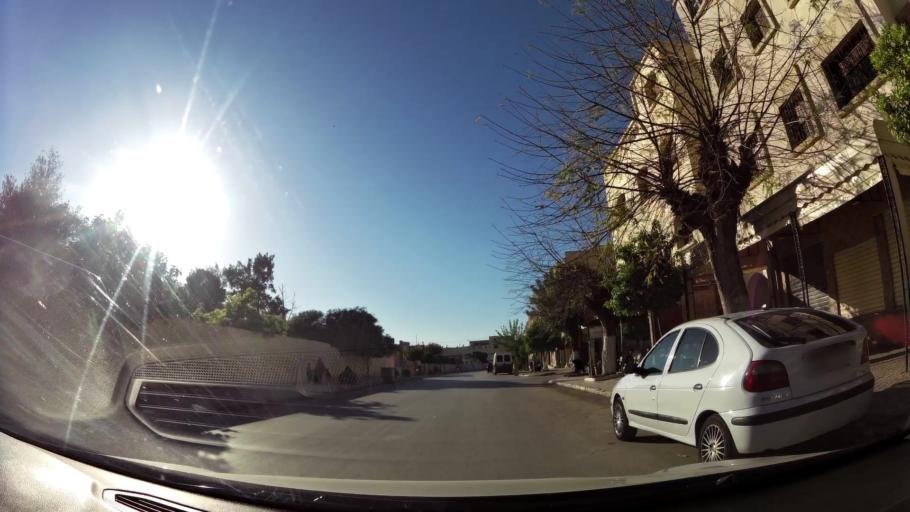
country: MA
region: Meknes-Tafilalet
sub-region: Meknes
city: Meknes
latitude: 33.8811
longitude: -5.5627
